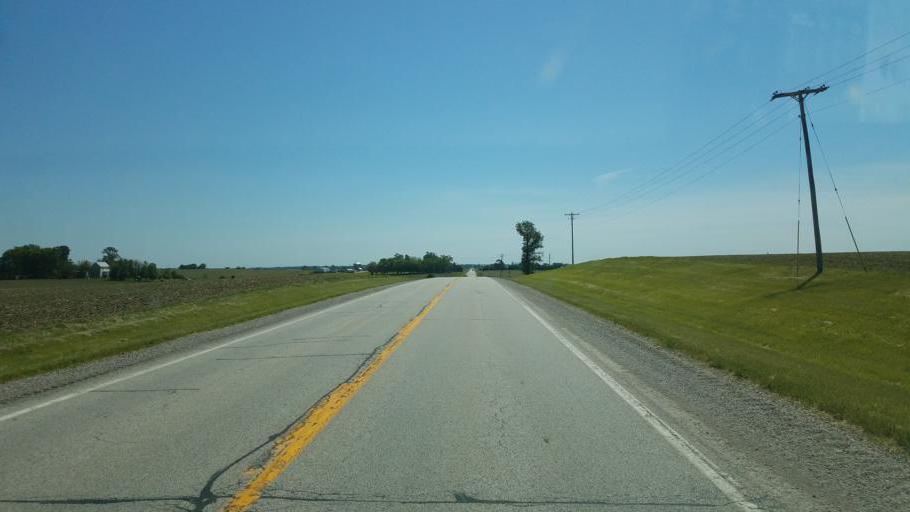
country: US
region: Illinois
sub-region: McLean County
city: Heyworth
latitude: 40.3119
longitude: -89.0726
